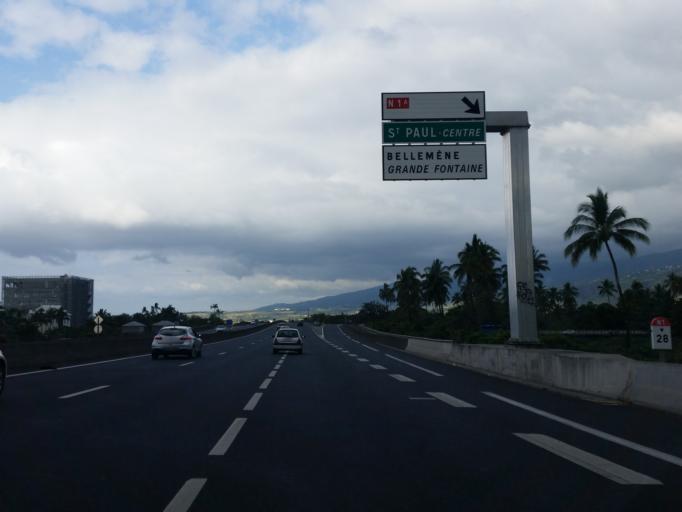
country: RE
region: Reunion
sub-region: Reunion
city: Saint-Paul
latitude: -21.0126
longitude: 55.2738
